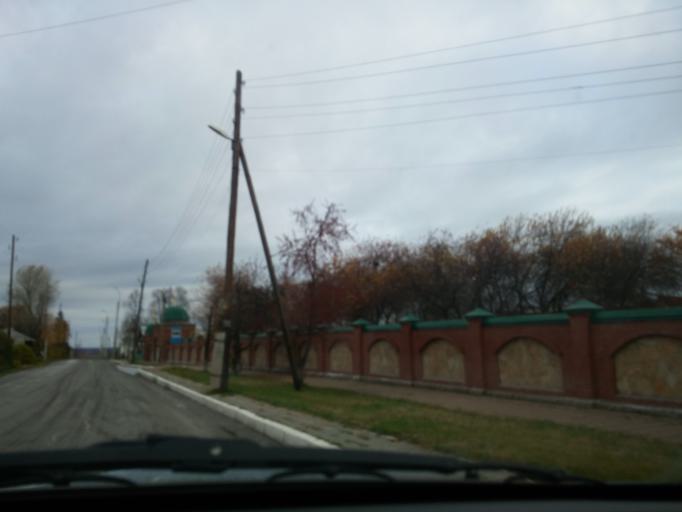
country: RU
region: Sverdlovsk
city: Turinsk
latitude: 58.0570
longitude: 63.6917
